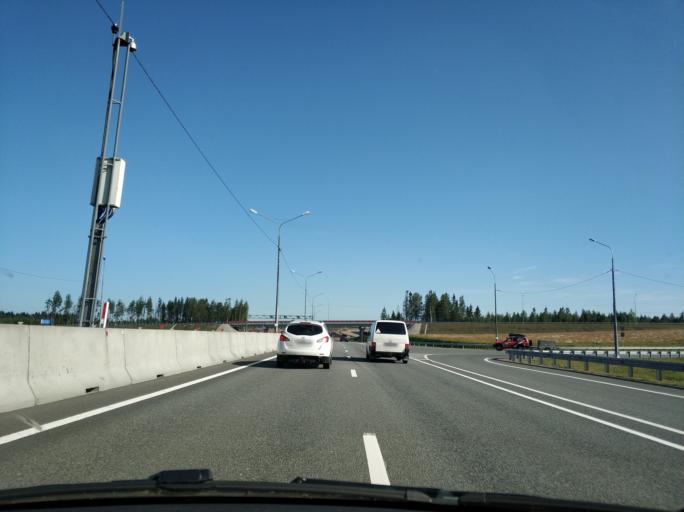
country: RU
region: Leningrad
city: Sosnovo
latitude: 60.5004
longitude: 30.1956
